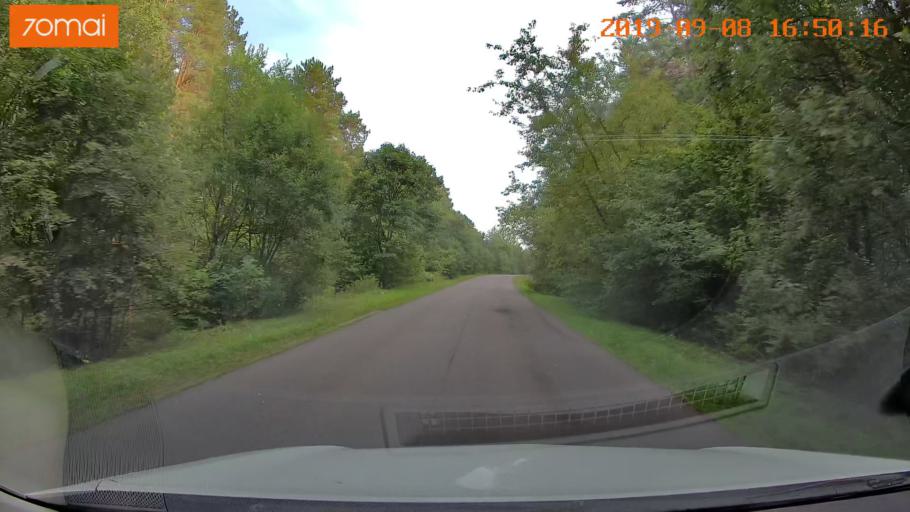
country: BY
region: Grodnenskaya
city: Hrodna
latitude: 53.8017
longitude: 23.8865
